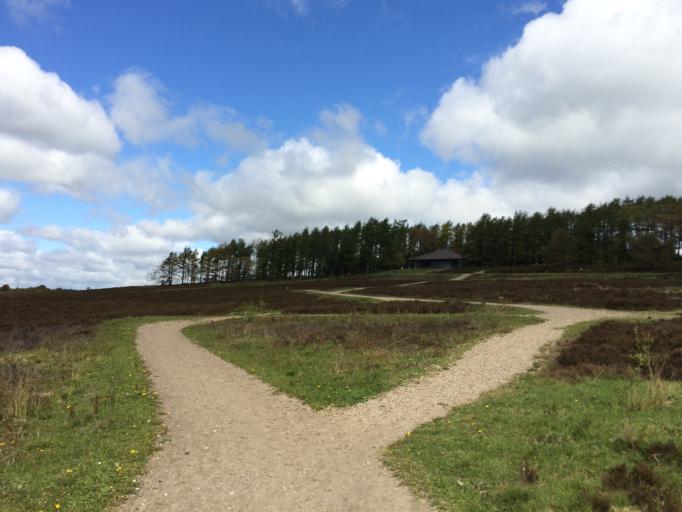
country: DK
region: Central Jutland
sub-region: Holstebro Kommune
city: Holstebro
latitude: 56.2290
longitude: 8.6206
